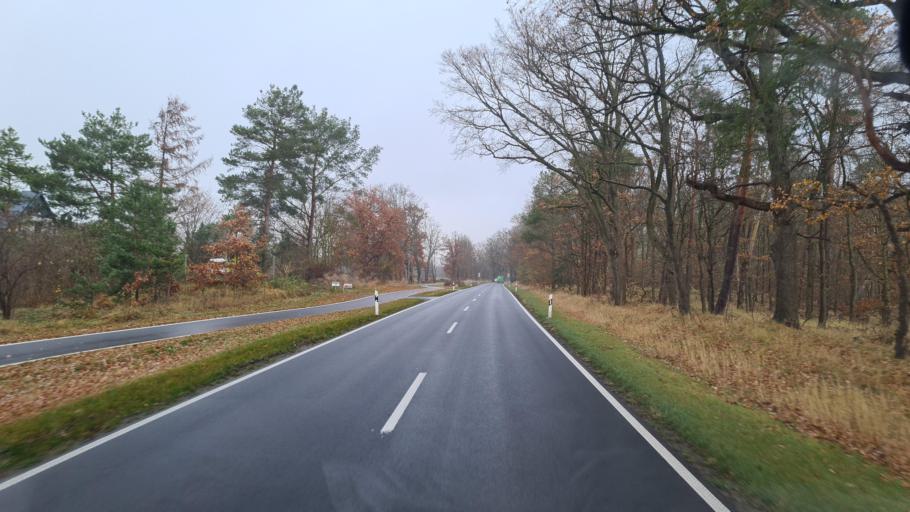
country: DE
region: Brandenburg
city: Gross Kreutz
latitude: 52.3906
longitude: 12.7656
